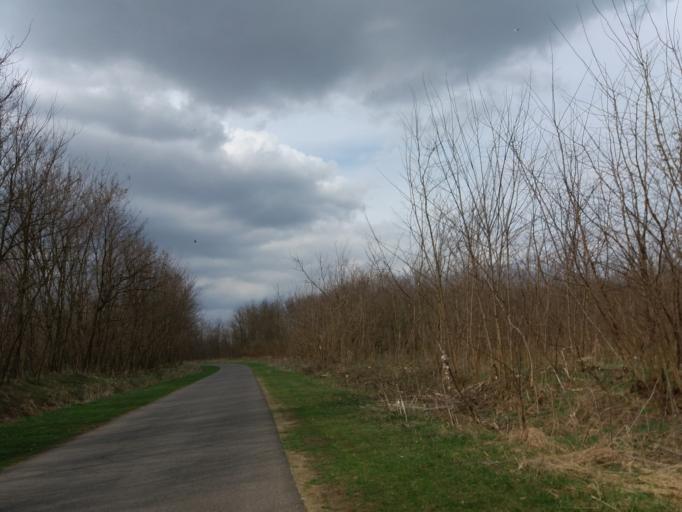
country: HU
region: Szabolcs-Szatmar-Bereg
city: Petnehaza
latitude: 48.0774
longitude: 22.0431
